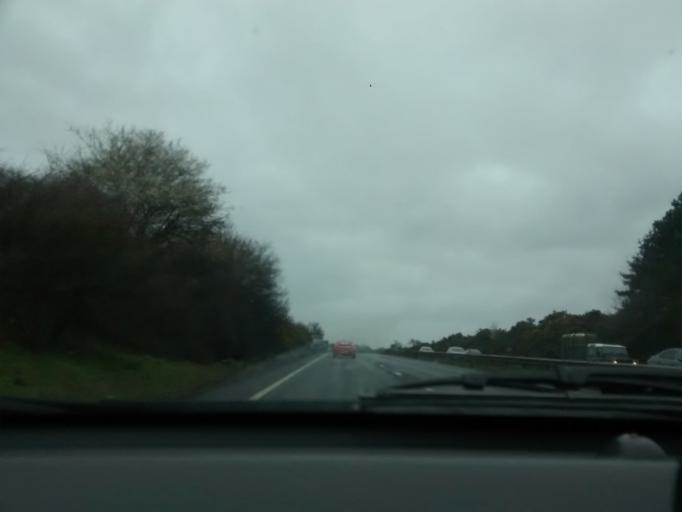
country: GB
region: England
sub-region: Suffolk
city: Kesgrave
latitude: 52.0453
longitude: 1.2704
